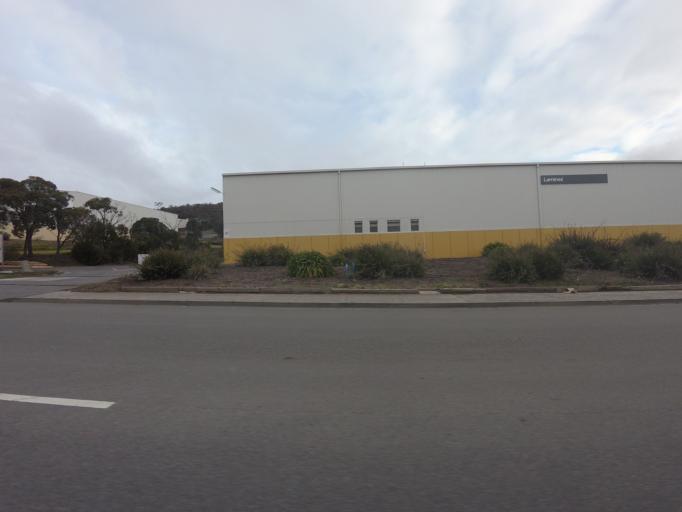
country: AU
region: Tasmania
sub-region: Clarence
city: Warrane
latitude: -42.8601
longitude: 147.3984
